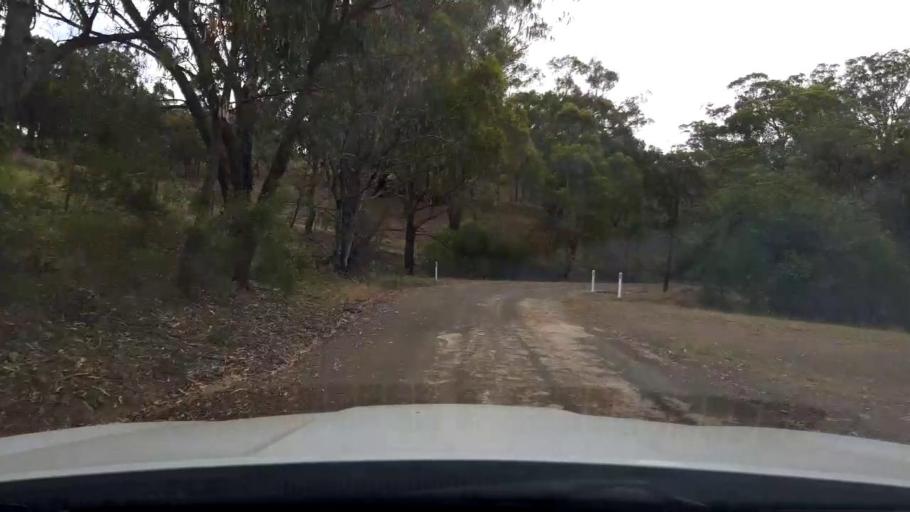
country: AU
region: Victoria
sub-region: Whittlesea
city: Whittlesea
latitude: -37.4908
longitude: 145.0592
